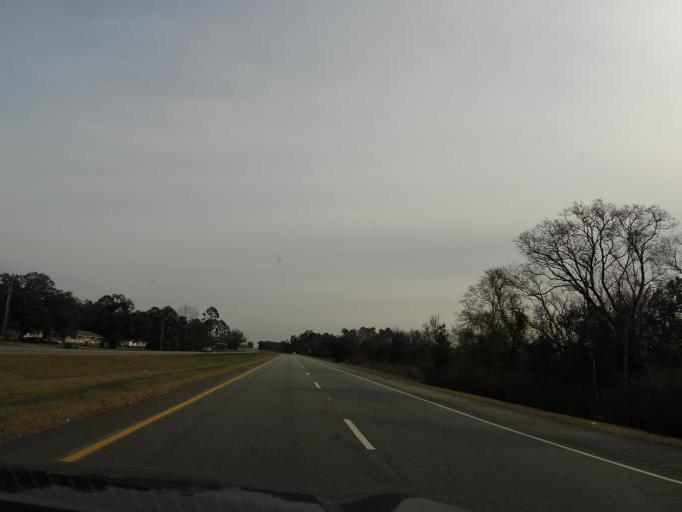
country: US
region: Georgia
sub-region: Seminole County
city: Donalsonville
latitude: 31.0879
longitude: -84.9887
